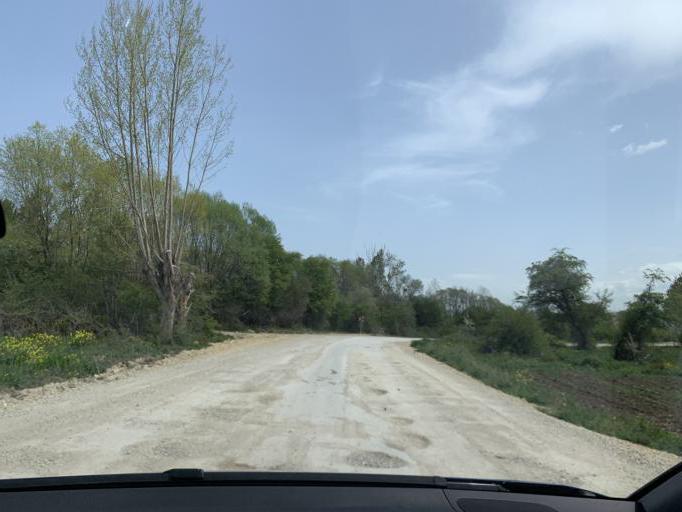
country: TR
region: Bolu
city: Bolu
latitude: 40.7607
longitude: 31.6955
